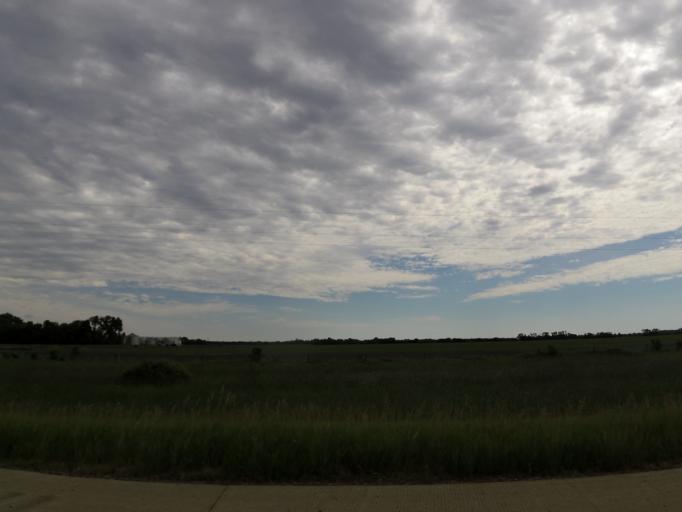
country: US
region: North Dakota
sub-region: Grand Forks County
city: Grand Forks
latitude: 48.1771
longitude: -97.1894
